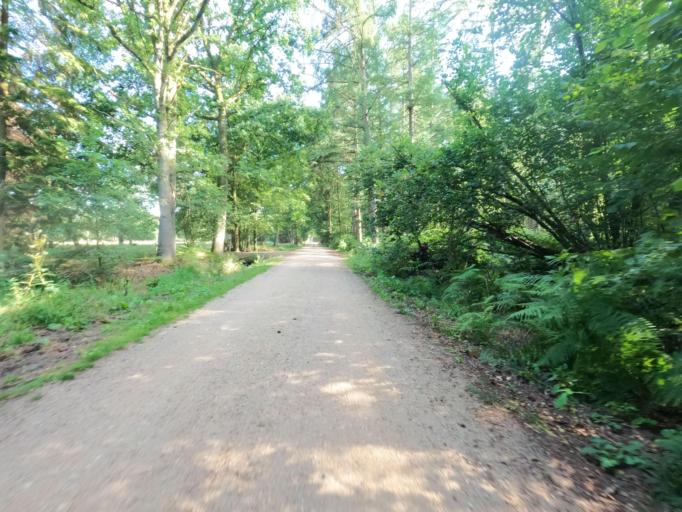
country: NL
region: Limburg
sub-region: Gemeente Beesel
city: Offenbeek
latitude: 51.2287
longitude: 6.0885
